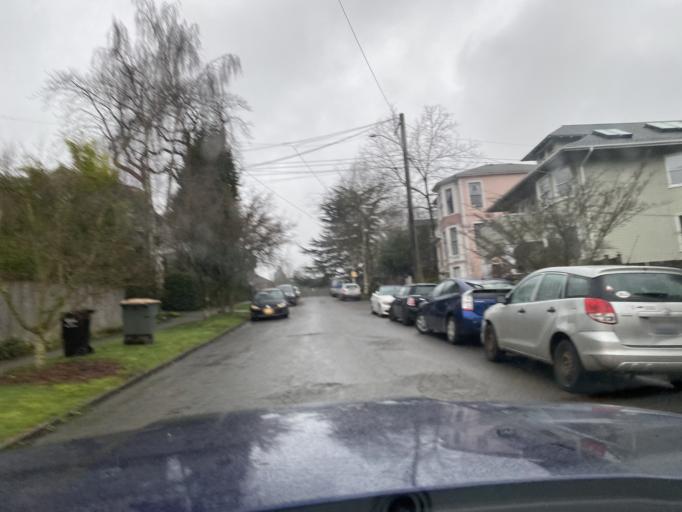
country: US
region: Washington
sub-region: King County
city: Seattle
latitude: 47.6306
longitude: -122.3089
